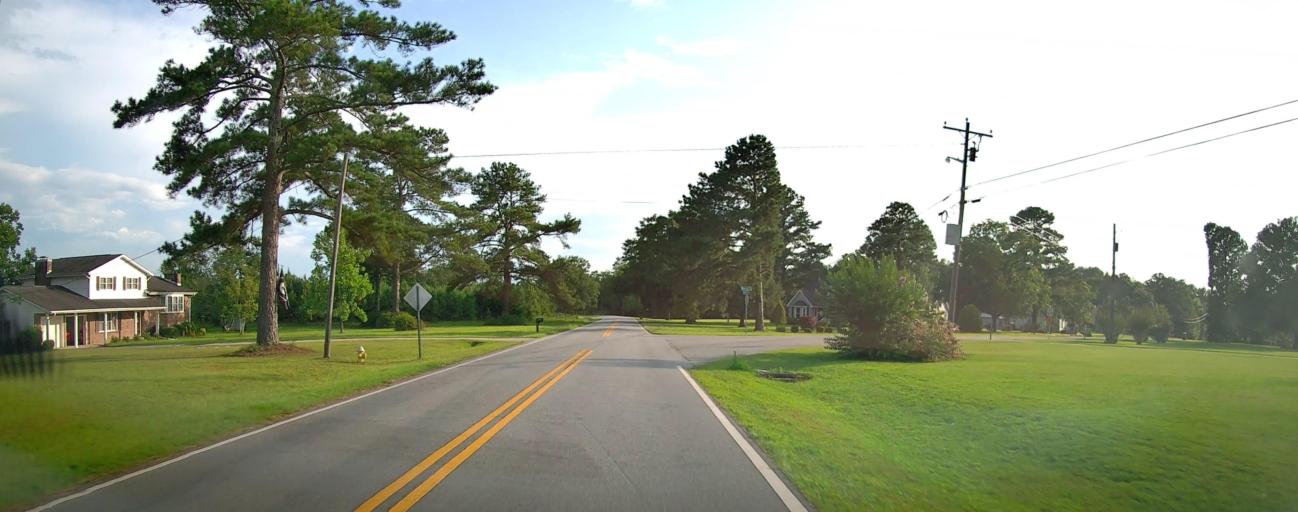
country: US
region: Georgia
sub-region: Peach County
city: Byron
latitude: 32.7336
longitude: -83.7393
